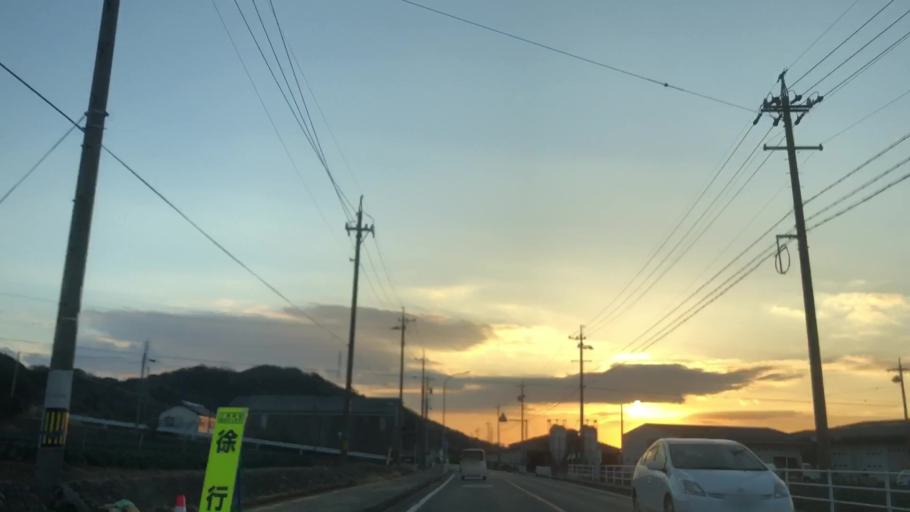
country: JP
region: Aichi
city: Toyohama
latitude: 34.6080
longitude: 137.0696
